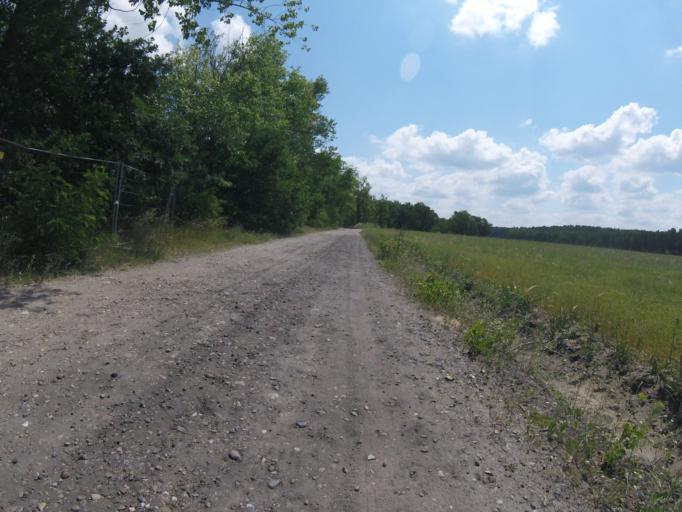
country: DE
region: Brandenburg
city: Bestensee
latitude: 52.2832
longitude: 13.6735
